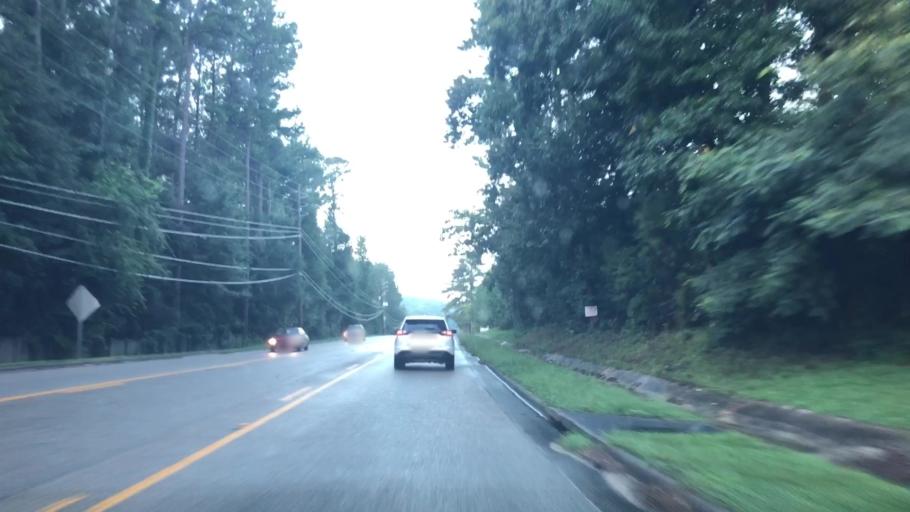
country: US
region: Alabama
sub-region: Shelby County
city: Indian Springs Village
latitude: 33.3683
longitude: -86.7608
